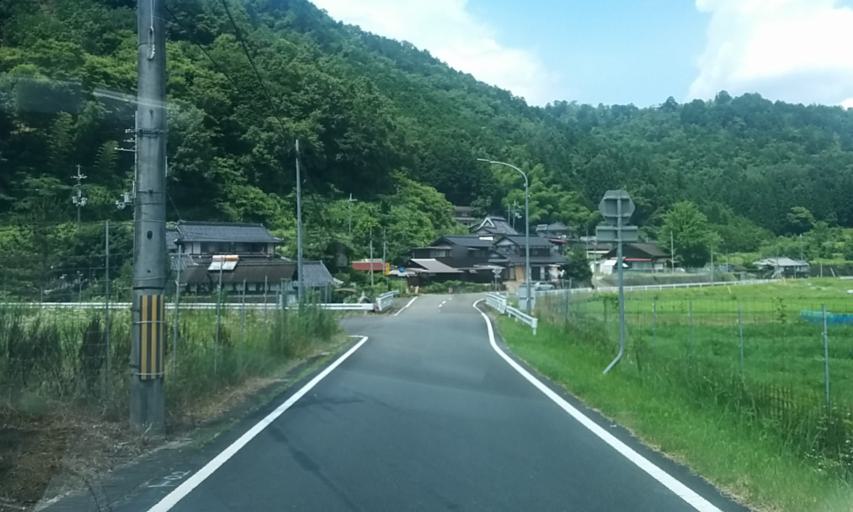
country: JP
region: Kyoto
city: Ayabe
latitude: 35.1926
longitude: 135.2170
